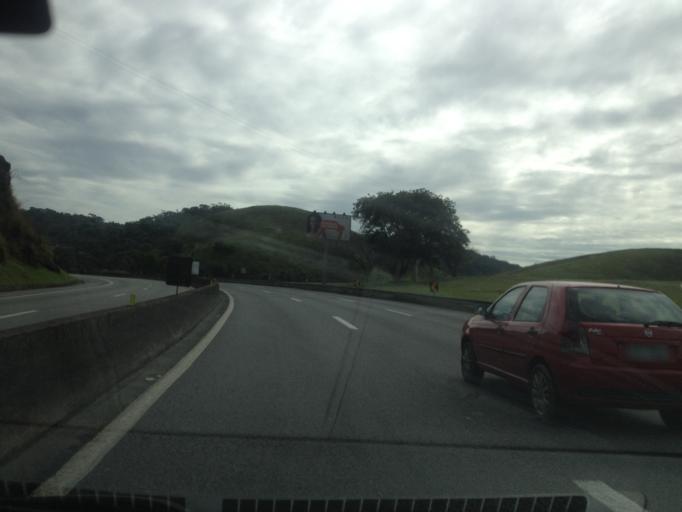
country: BR
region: Rio de Janeiro
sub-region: Pirai
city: Pirai
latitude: -22.6105
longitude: -43.9316
